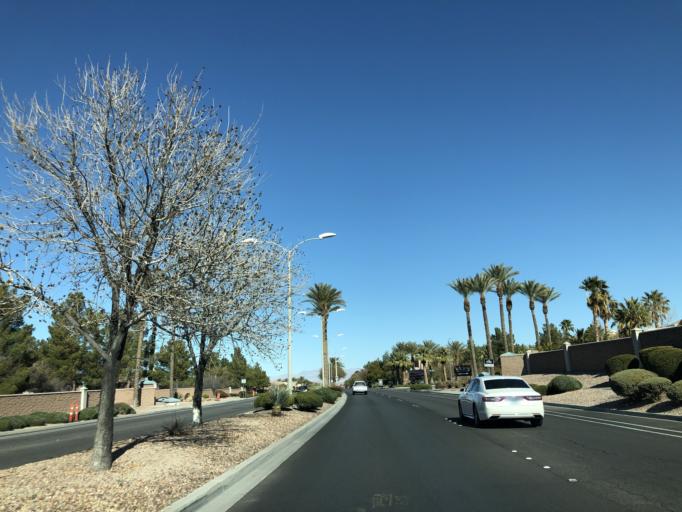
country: US
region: Nevada
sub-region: Clark County
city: Whitney
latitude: 36.0080
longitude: -115.0668
